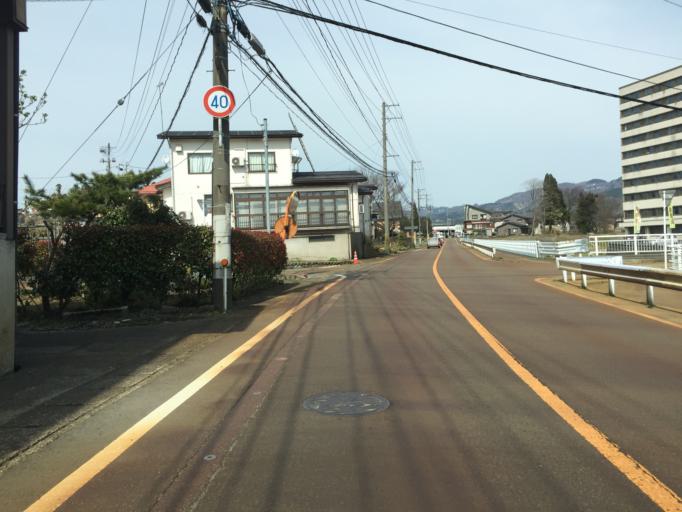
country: JP
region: Niigata
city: Ojiya
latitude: 37.3284
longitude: 138.8054
